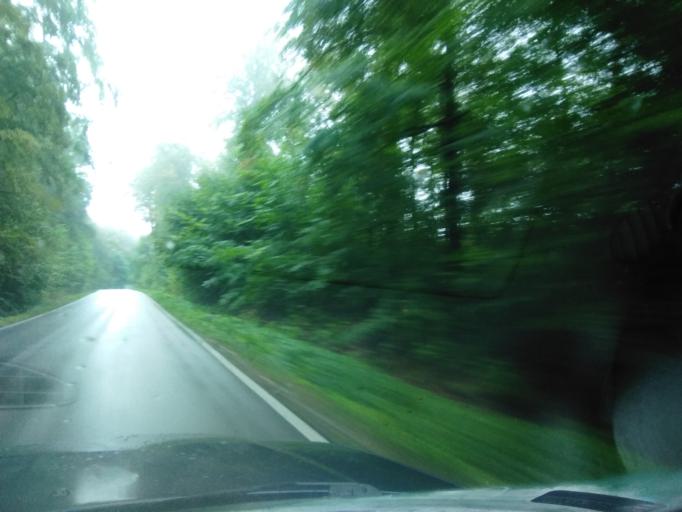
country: PL
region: Subcarpathian Voivodeship
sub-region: Powiat ropczycko-sedziszowski
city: Niedzwiada
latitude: 50.0521
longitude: 21.5347
